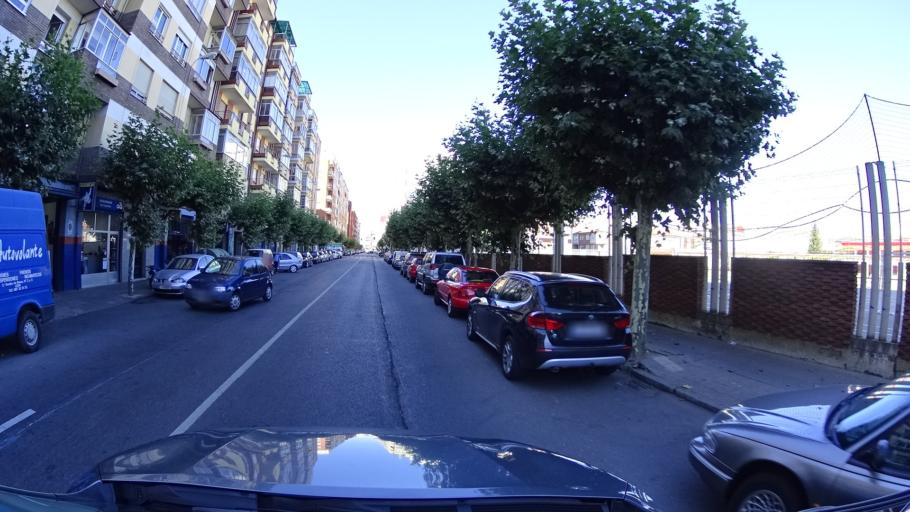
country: ES
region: Castille and Leon
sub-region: Provincia de Leon
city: Leon
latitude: 42.5938
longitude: -5.5602
